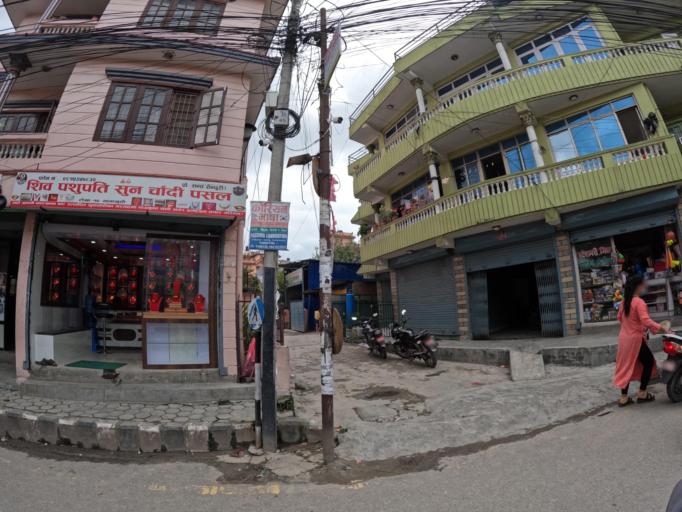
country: NP
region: Central Region
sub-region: Bagmati Zone
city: Kathmandu
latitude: 27.7372
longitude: 85.3169
